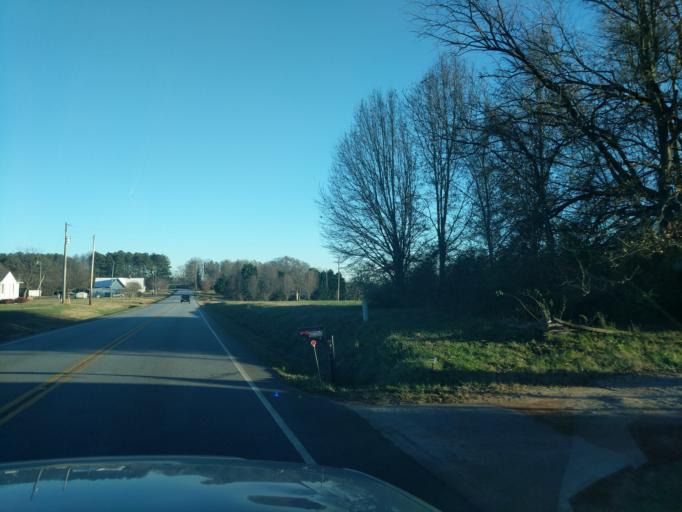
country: US
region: South Carolina
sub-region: Oconee County
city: Seneca
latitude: 34.5976
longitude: -83.0076
